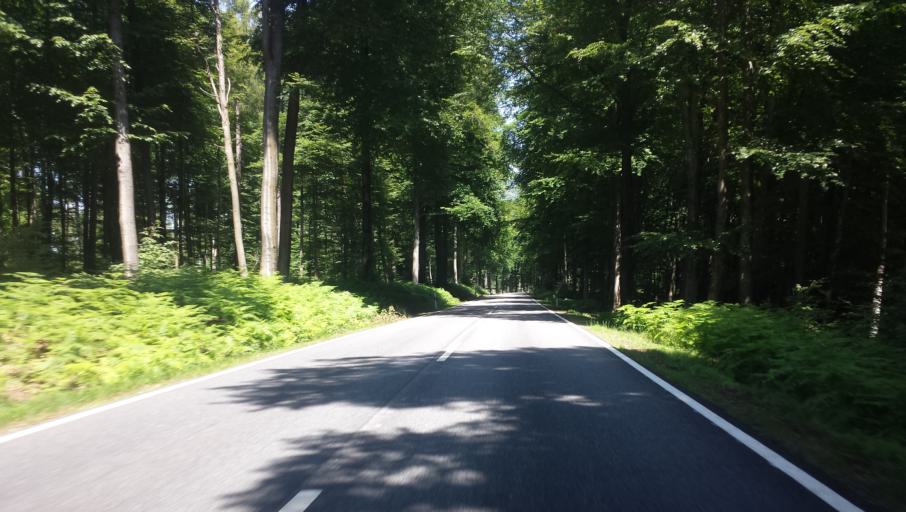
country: DE
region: Rheinland-Pfalz
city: Waldleiningen
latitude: 49.3655
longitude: 7.8489
